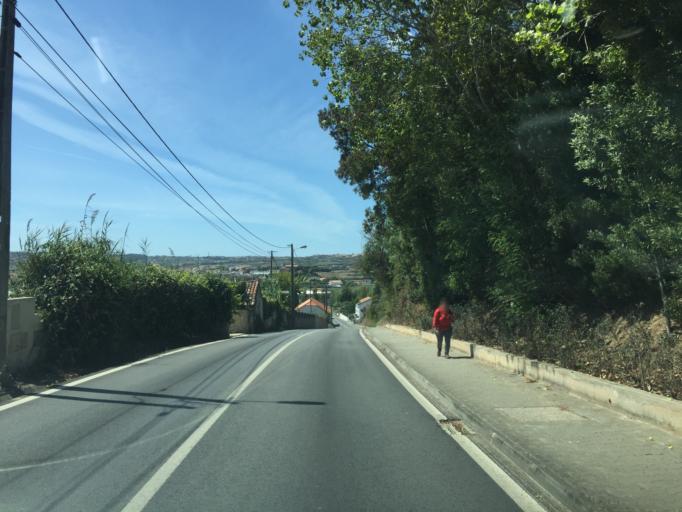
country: PT
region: Lisbon
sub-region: Lourinha
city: Lourinha
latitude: 39.2536
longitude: -9.3128
